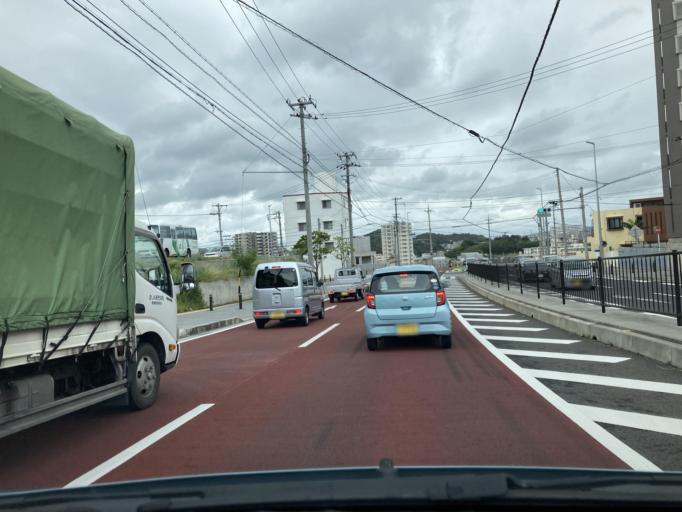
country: JP
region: Okinawa
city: Naha-shi
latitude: 26.2007
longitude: 127.7296
